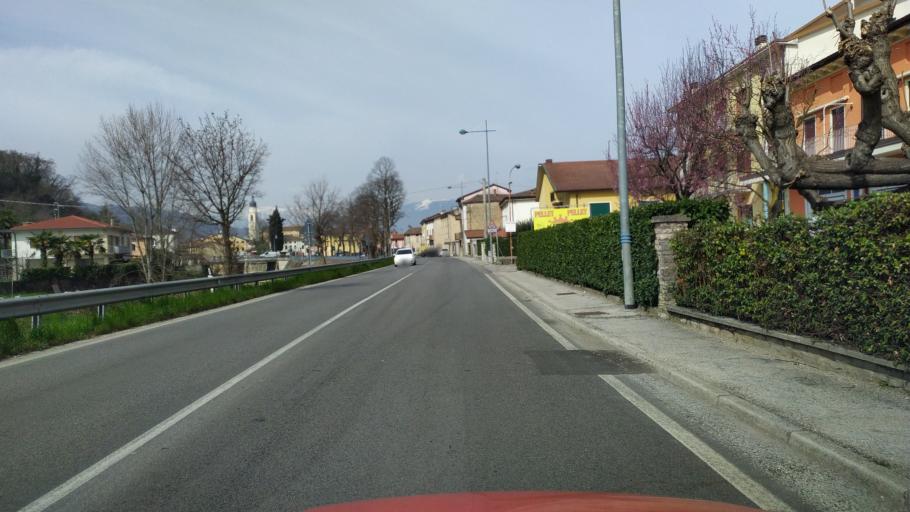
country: IT
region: Veneto
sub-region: Provincia di Vicenza
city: Isola Vicentina
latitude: 45.6264
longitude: 11.4474
